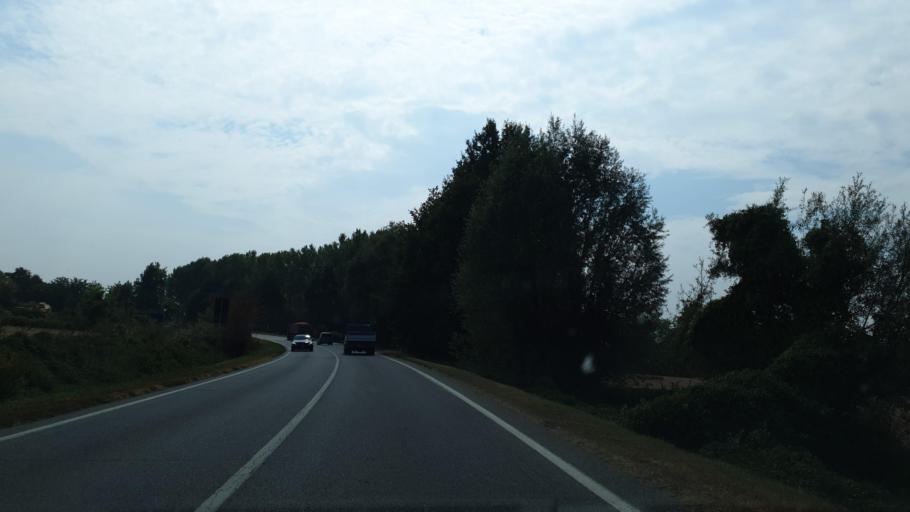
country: IT
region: Lombardy
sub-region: Provincia di Cremona
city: San Daniele Po
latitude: 45.0840
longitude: 10.1784
